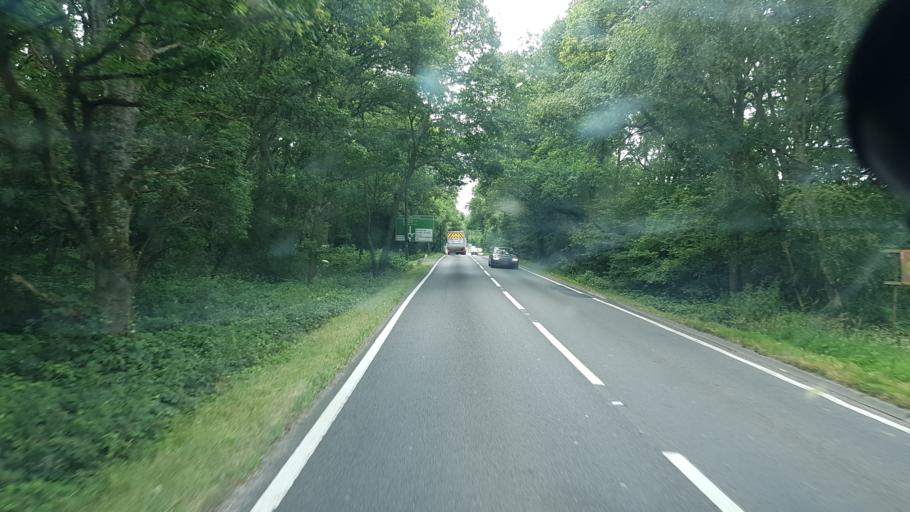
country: GB
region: England
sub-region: Surrey
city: Felbridge
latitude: 51.1667
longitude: -0.0499
